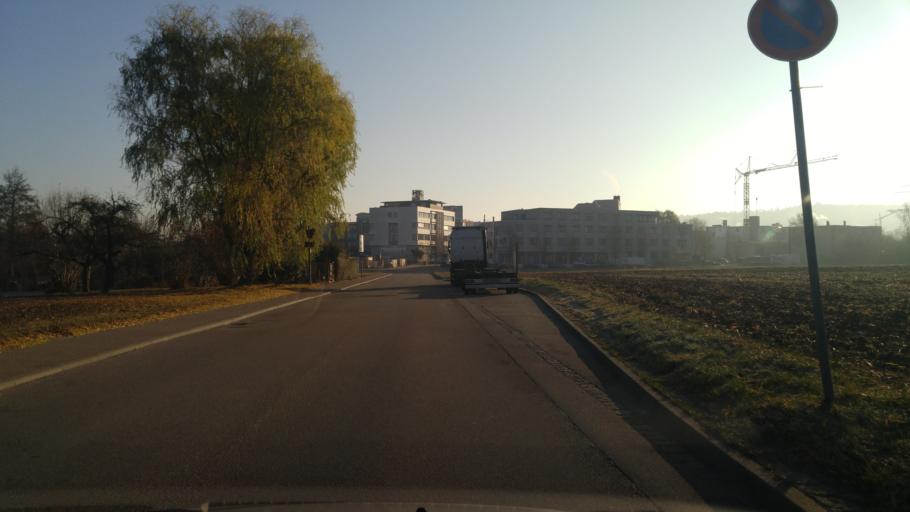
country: DE
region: Baden-Wuerttemberg
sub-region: Regierungsbezirk Stuttgart
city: Gerlingen
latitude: 48.8073
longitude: 9.0689
